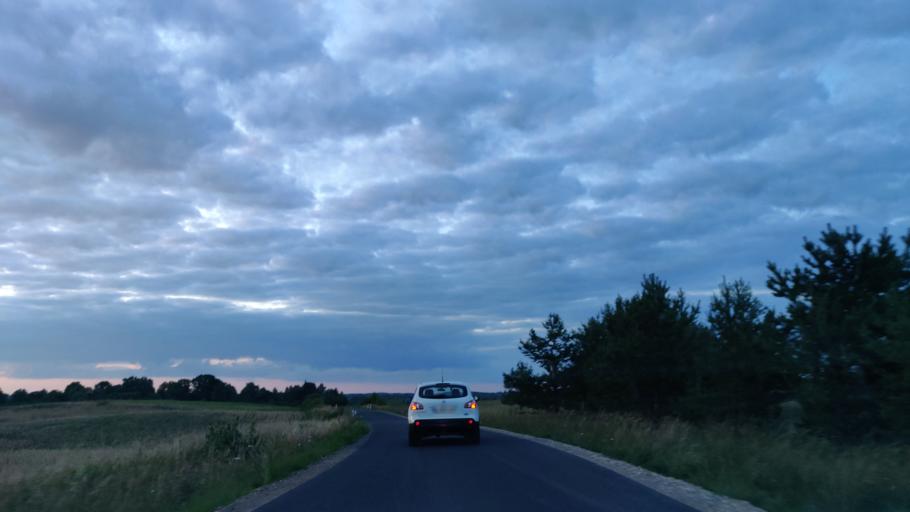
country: LT
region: Vilnius County
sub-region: Trakai
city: Rudiskes
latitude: 54.6194
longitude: 24.8136
